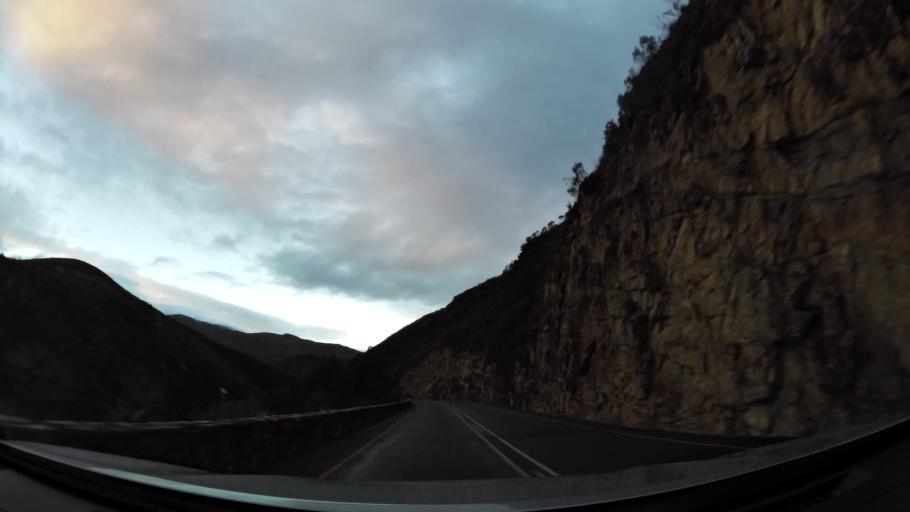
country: ZA
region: Western Cape
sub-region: Overberg District Municipality
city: Swellendam
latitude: -33.9903
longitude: 20.7085
